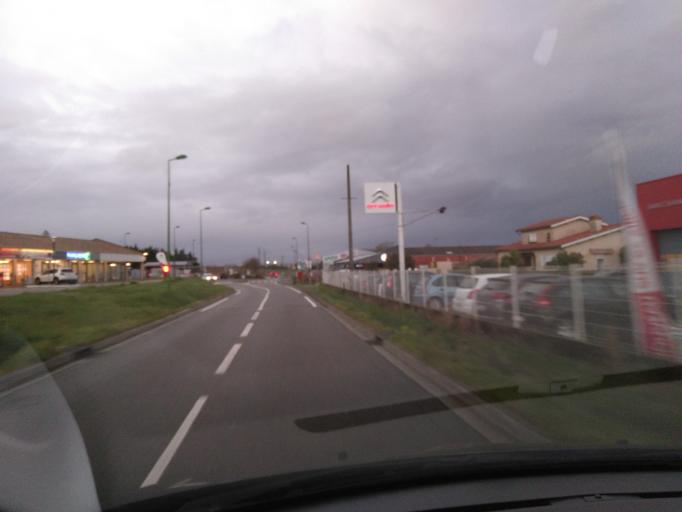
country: FR
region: Midi-Pyrenees
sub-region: Departement de la Haute-Garonne
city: Aussonne
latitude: 43.6876
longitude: 1.3362
